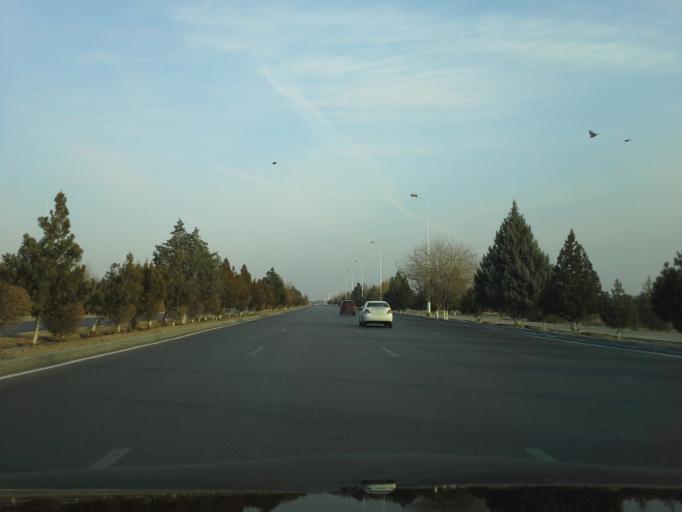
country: TM
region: Ahal
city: Abadan
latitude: 38.0387
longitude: 58.2145
